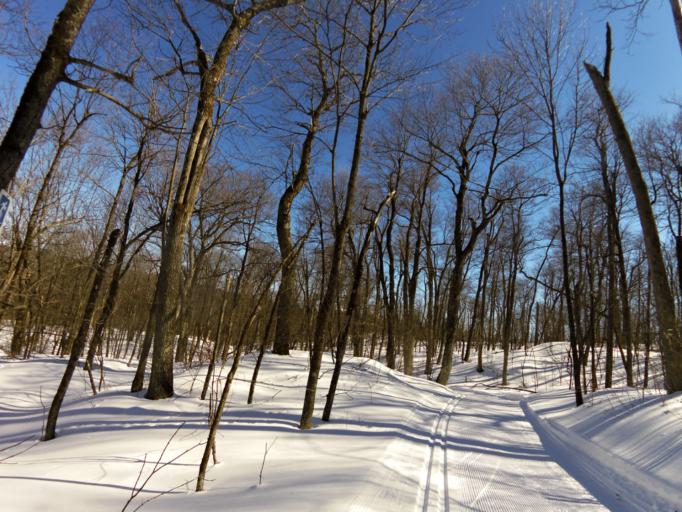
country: CA
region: Quebec
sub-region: Outaouais
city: Gatineau
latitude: 45.5051
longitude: -75.8640
